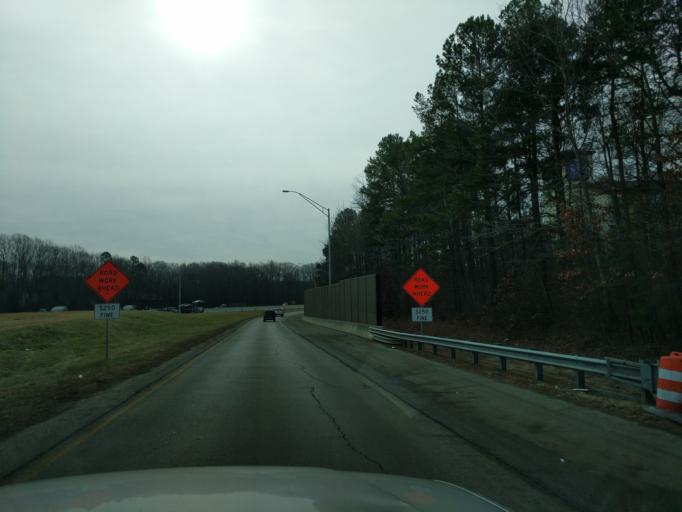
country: US
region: North Carolina
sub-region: Mecklenburg County
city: Charlotte
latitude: 35.3062
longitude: -80.8501
